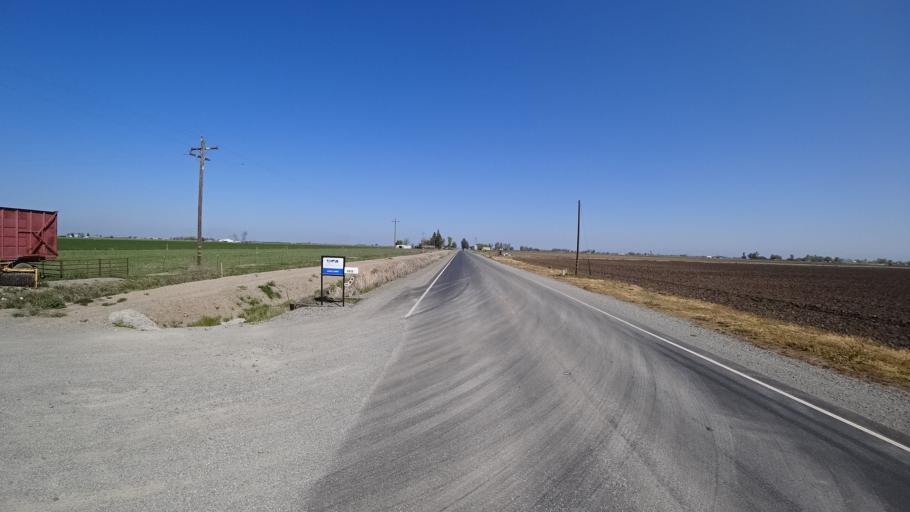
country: US
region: California
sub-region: Glenn County
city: Willows
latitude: 39.5745
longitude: -122.0652
